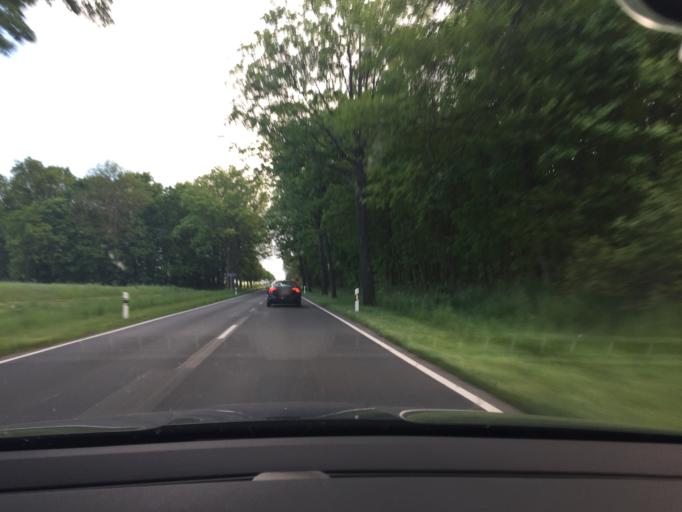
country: DE
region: Saxony-Anhalt
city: Kropstadt
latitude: 52.0298
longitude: 12.8011
